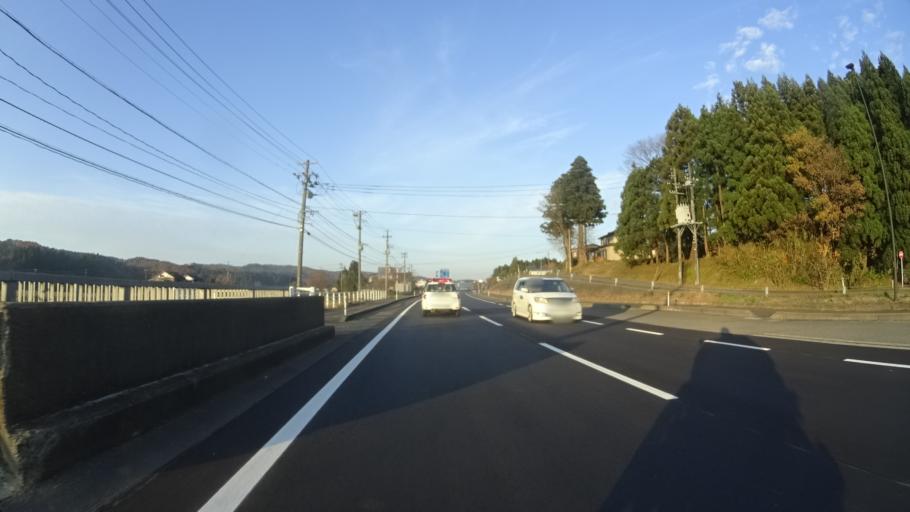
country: JP
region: Niigata
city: Nagaoka
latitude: 37.4455
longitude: 138.7433
